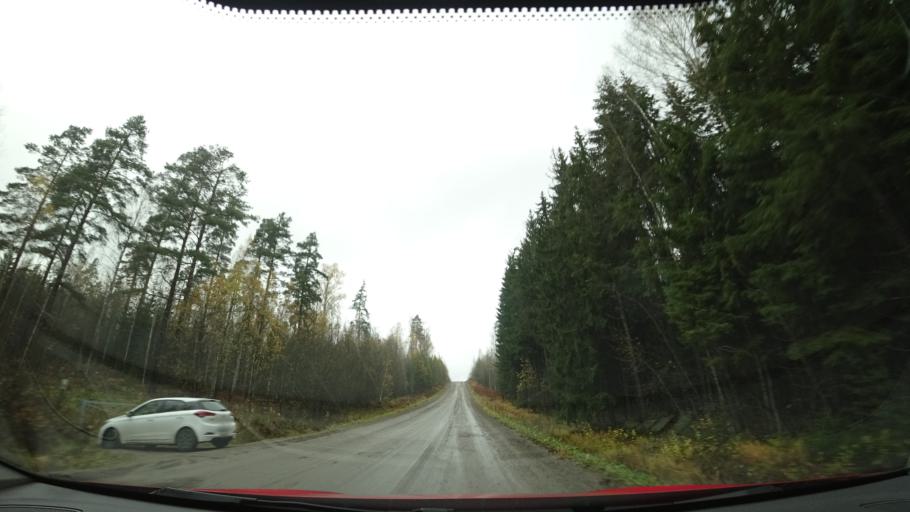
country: FI
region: Uusimaa
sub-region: Helsinki
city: Sibbo
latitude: 60.2962
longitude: 25.2000
